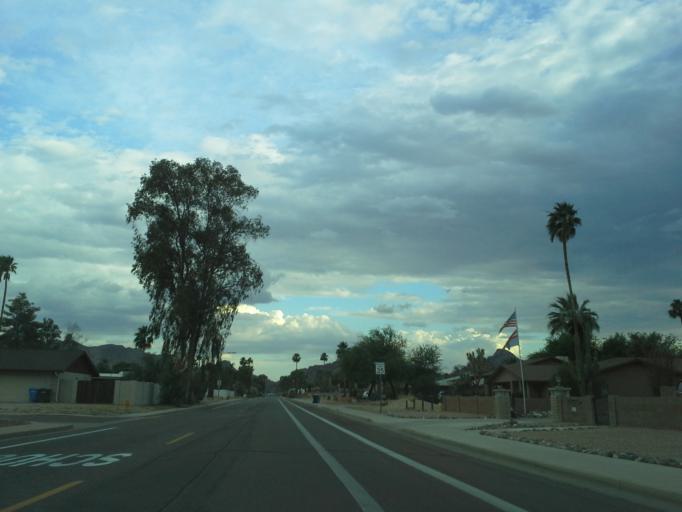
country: US
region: Arizona
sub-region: Maricopa County
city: Paradise Valley
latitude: 33.5887
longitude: -112.0045
